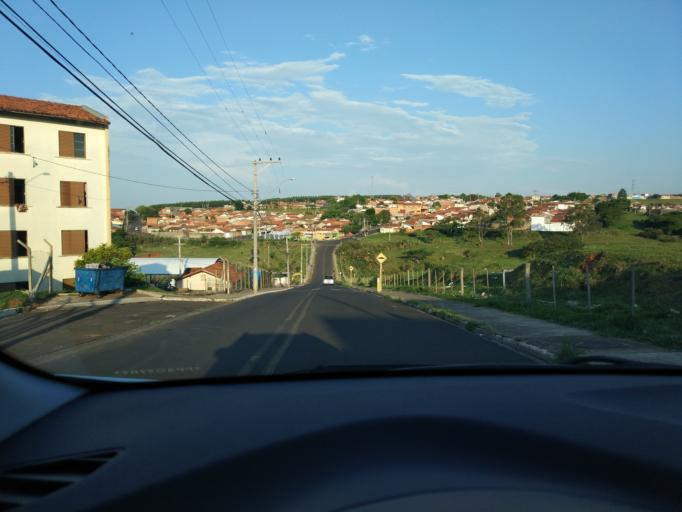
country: BR
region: Sao Paulo
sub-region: Botucatu
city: Botucatu
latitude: -22.8984
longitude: -48.4335
